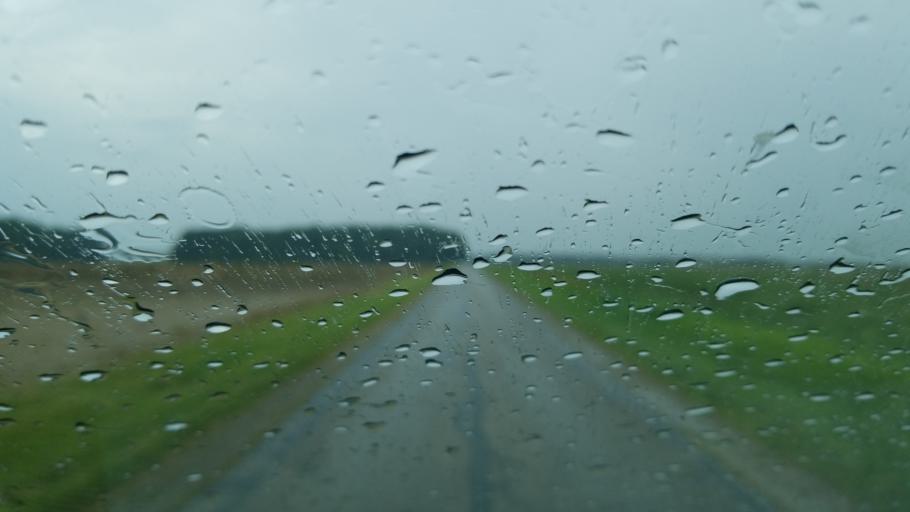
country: US
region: Ohio
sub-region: Huron County
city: Willard
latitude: 41.0108
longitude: -82.8167
